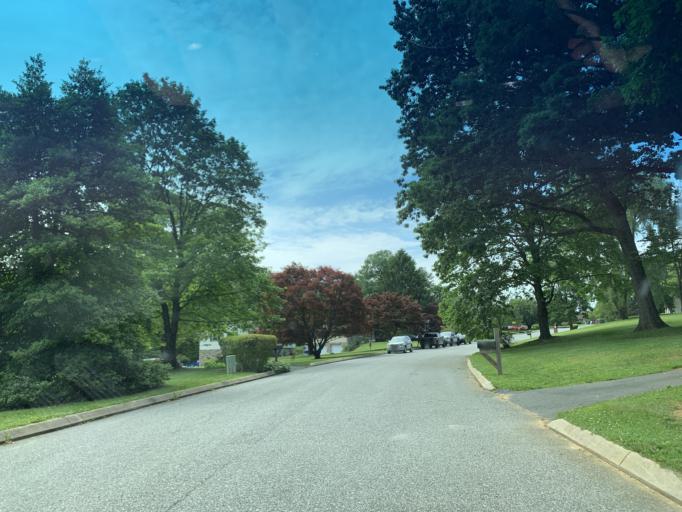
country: US
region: Maryland
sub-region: Harford County
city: Jarrettsville
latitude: 39.6249
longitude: -76.4644
